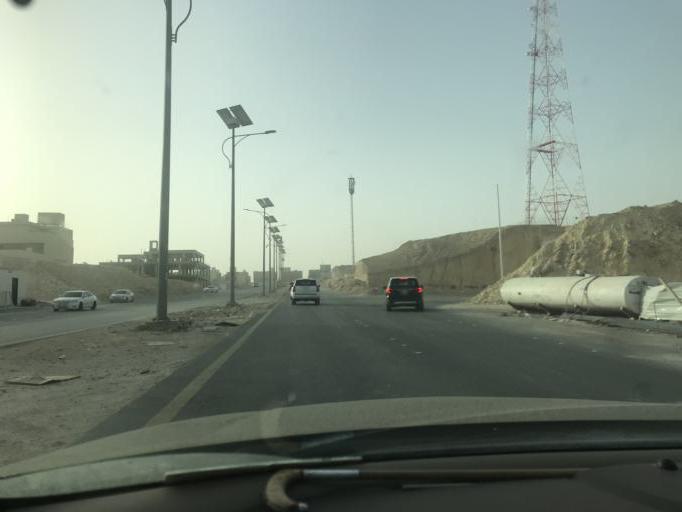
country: SA
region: Ar Riyad
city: Riyadh
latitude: 24.8404
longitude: 46.6669
